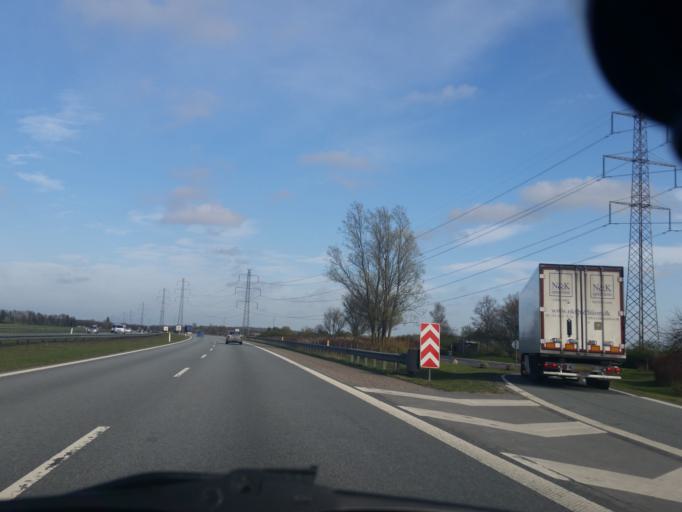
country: DK
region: Zealand
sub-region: Ringsted Kommune
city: Ringsted
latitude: 55.4534
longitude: 11.8534
